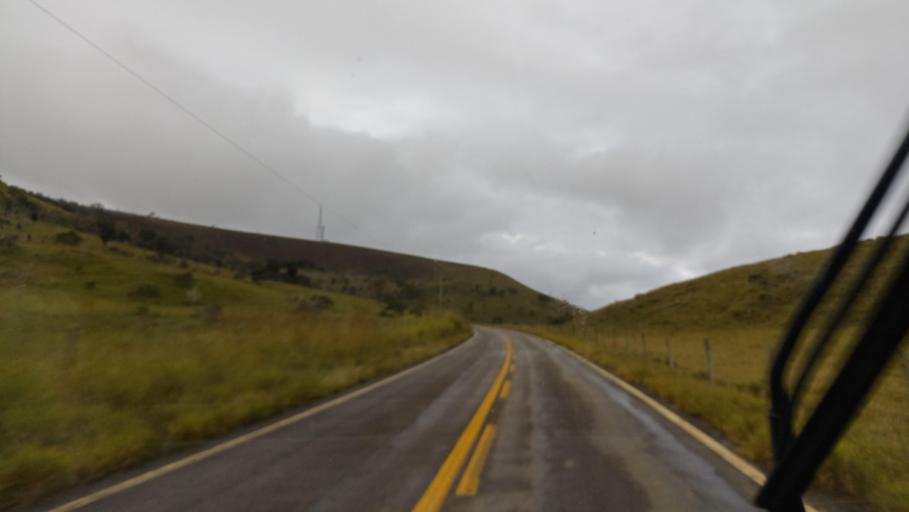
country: BR
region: Minas Gerais
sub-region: Joaima
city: Joaima
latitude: -16.6762
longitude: -40.5252
